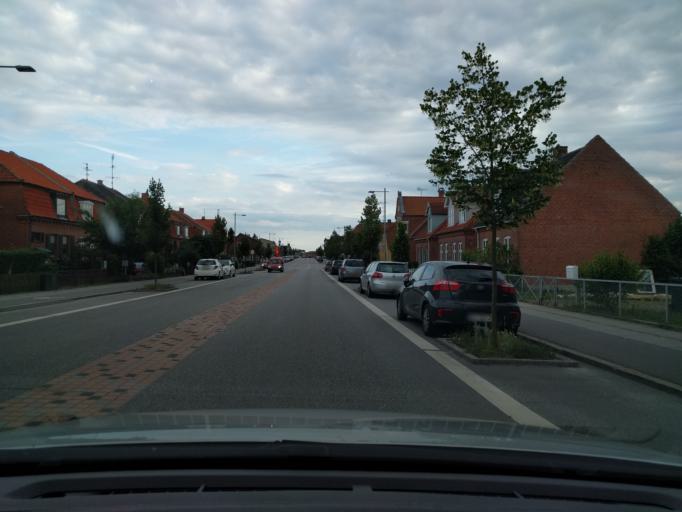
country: DK
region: Zealand
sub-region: Guldborgsund Kommune
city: Nykobing Falster
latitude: 54.7795
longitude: 11.8669
